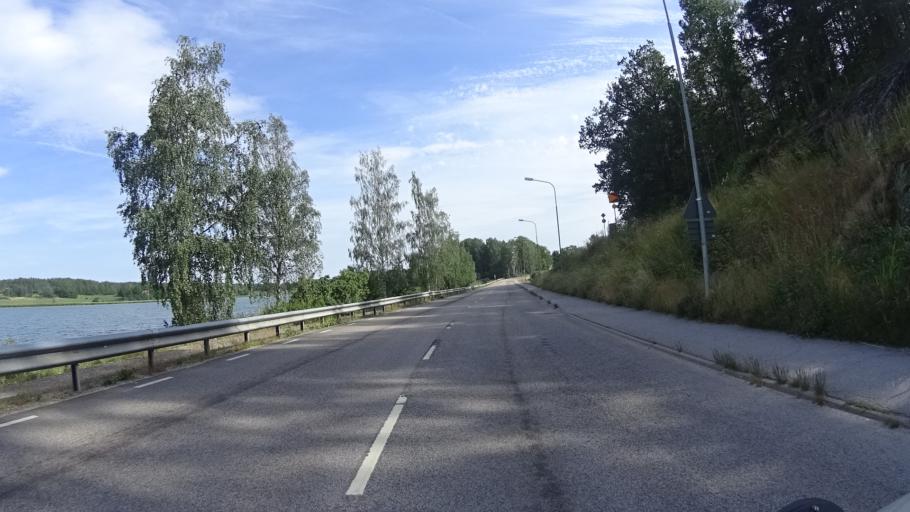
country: SE
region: Kalmar
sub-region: Vasterviks Kommun
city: Gamleby
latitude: 57.8945
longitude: 16.4149
